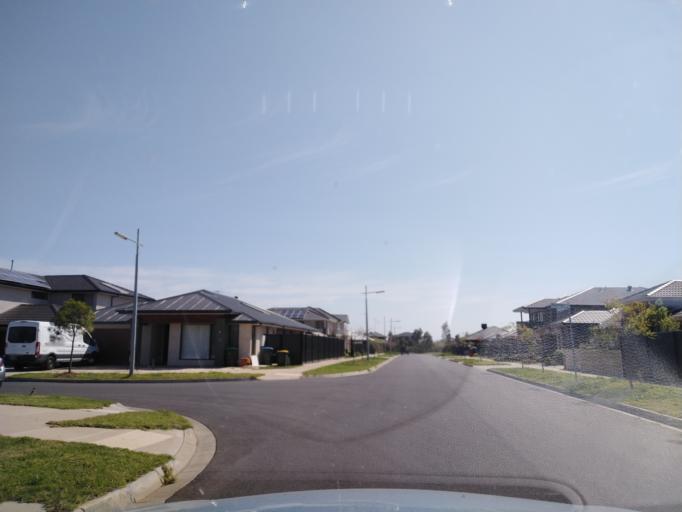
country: AU
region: Victoria
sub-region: Wyndham
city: Williams Landing
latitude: -37.8405
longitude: 144.7412
